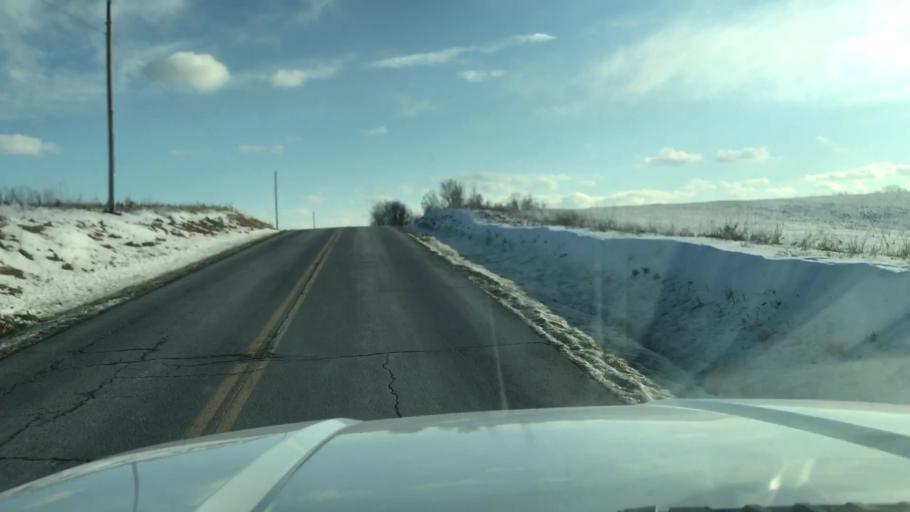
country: US
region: Missouri
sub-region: Holt County
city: Oregon
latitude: 40.0532
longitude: -94.9750
